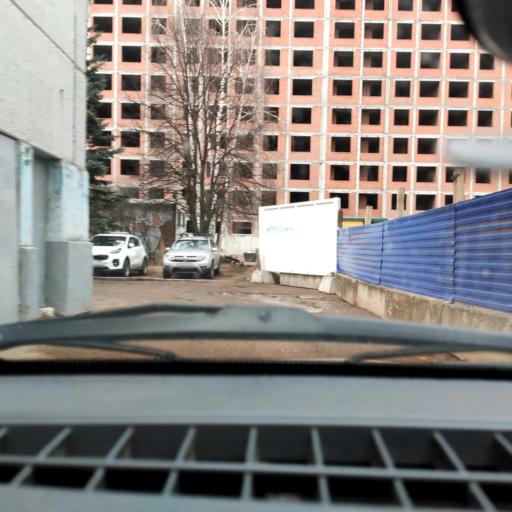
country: RU
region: Bashkortostan
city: Ufa
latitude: 54.7142
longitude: 56.0122
